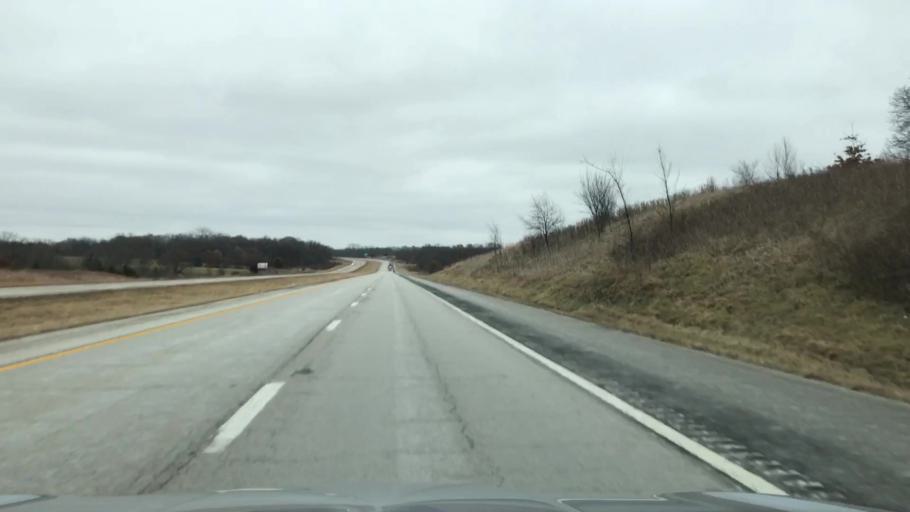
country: US
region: Missouri
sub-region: Caldwell County
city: Hamilton
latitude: 39.7404
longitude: -94.0359
